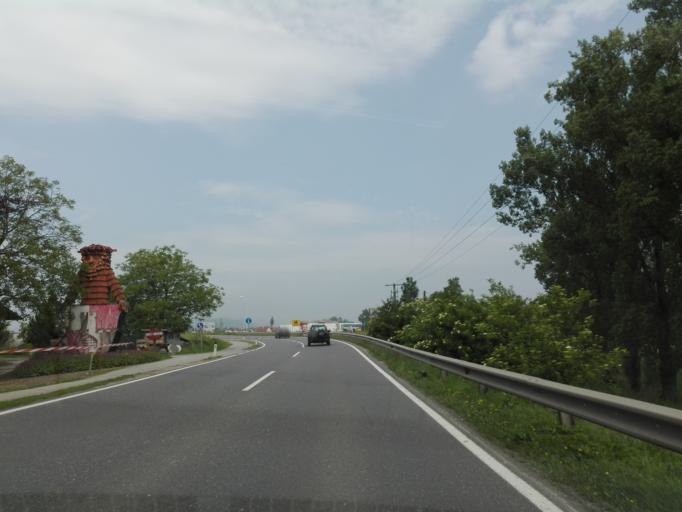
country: AT
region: Upper Austria
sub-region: Politischer Bezirk Urfahr-Umgebung
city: Feldkirchen an der Donau
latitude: 48.2960
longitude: 14.0348
